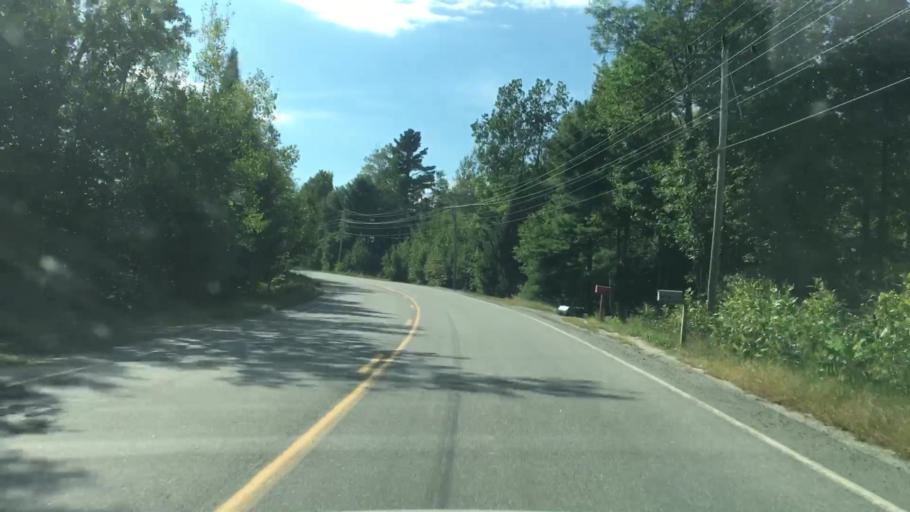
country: US
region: Maine
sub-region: Penobscot County
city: Lincoln
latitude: 45.3934
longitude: -68.5265
